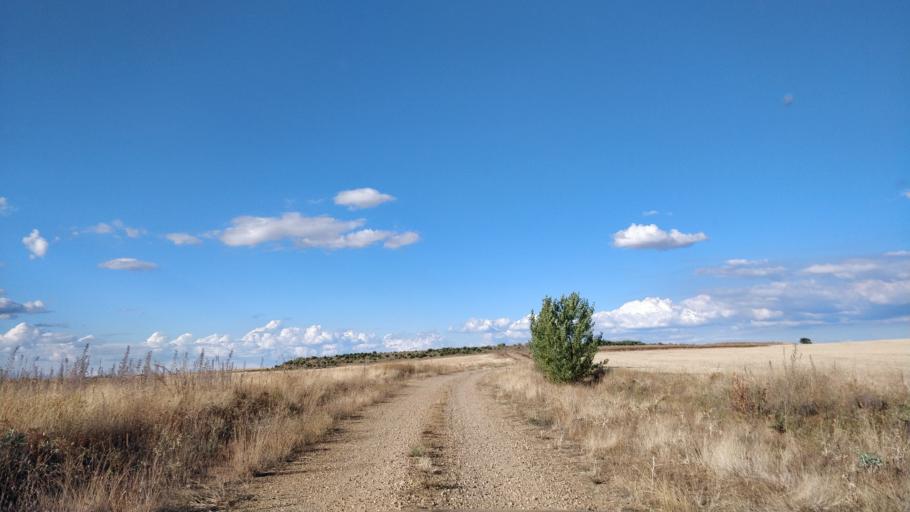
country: ES
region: Castille and Leon
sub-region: Provincia de Leon
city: Santa Cristina de Valmadrigal
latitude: 42.3420
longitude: -5.2709
